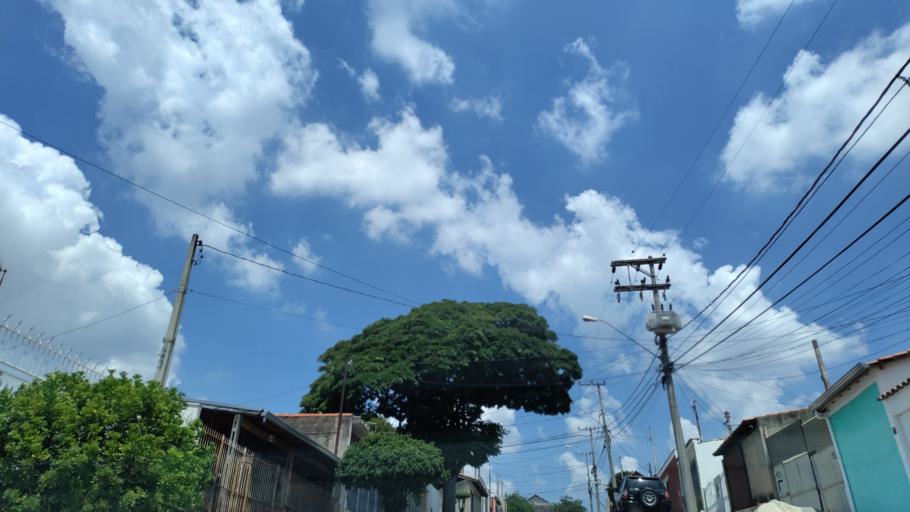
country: BR
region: Sao Paulo
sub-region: Sorocaba
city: Sorocaba
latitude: -23.4853
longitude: -47.4638
